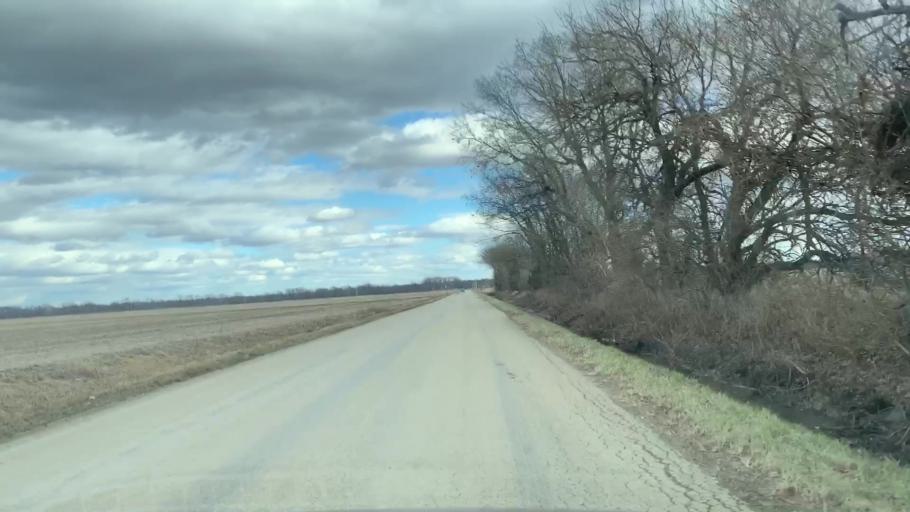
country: US
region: Kansas
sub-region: Allen County
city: Humboldt
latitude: 37.8130
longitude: -95.4686
